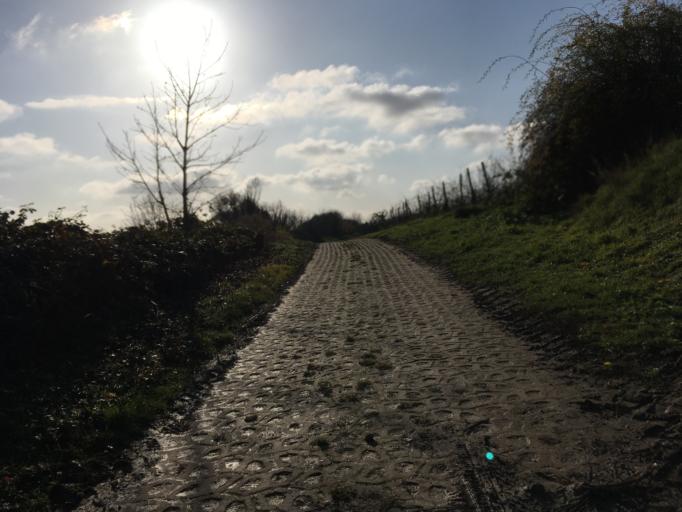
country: DE
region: Rheinland-Pfalz
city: Bodenheim
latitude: 49.9508
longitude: 8.3042
